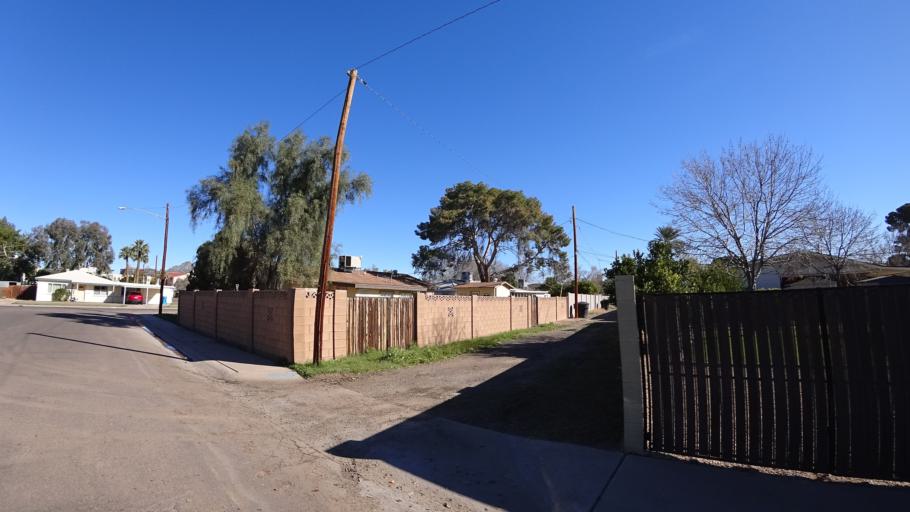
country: US
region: Arizona
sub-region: Maricopa County
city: Phoenix
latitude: 33.5002
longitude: -112.0316
